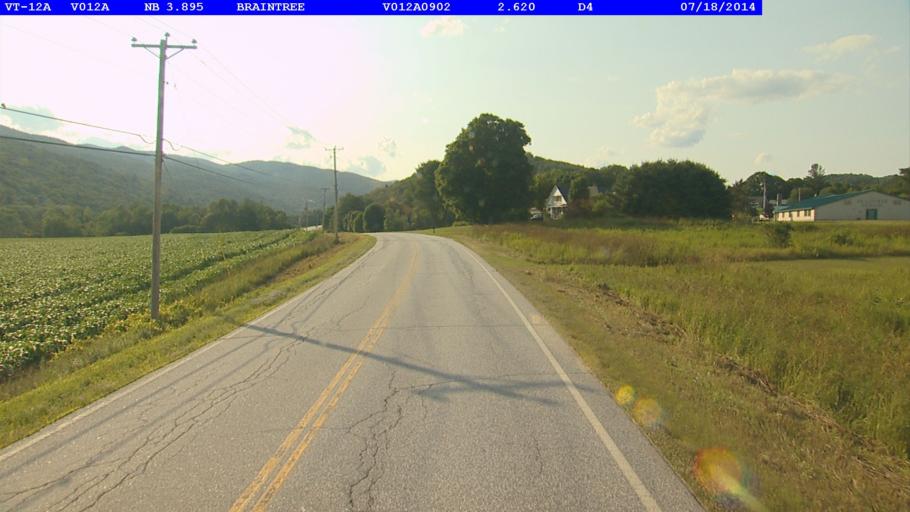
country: US
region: Vermont
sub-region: Orange County
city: Randolph
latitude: 43.9540
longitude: -72.7219
